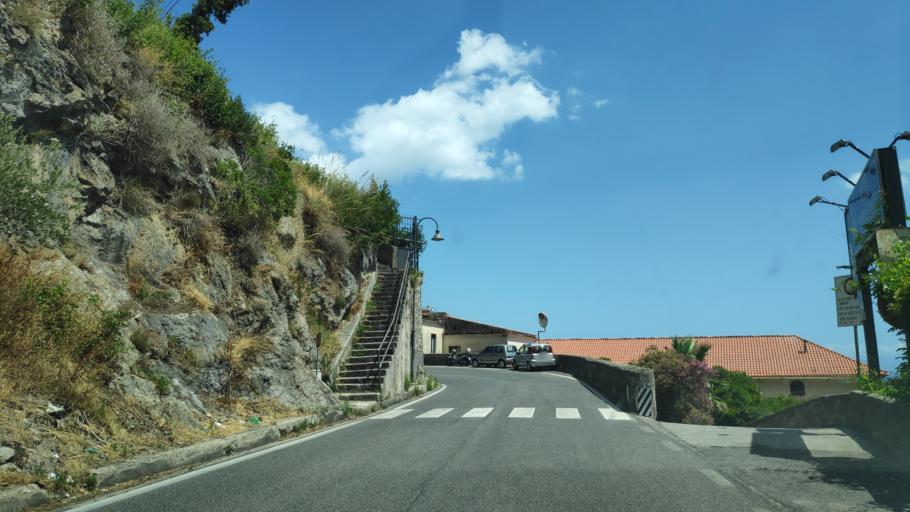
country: IT
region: Campania
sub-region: Provincia di Salerno
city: Ravello
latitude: 40.6462
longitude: 14.6189
